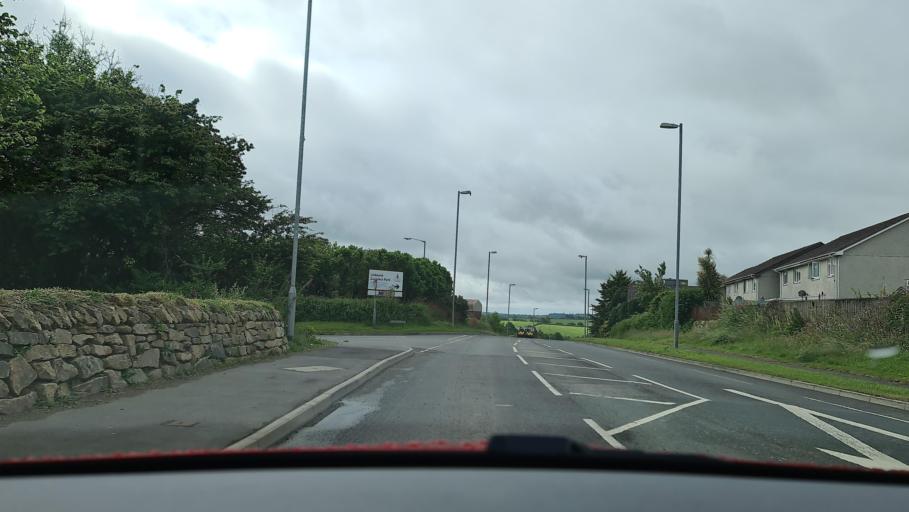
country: GB
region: England
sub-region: Cornwall
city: Liskeard
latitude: 50.4593
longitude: -4.4508
